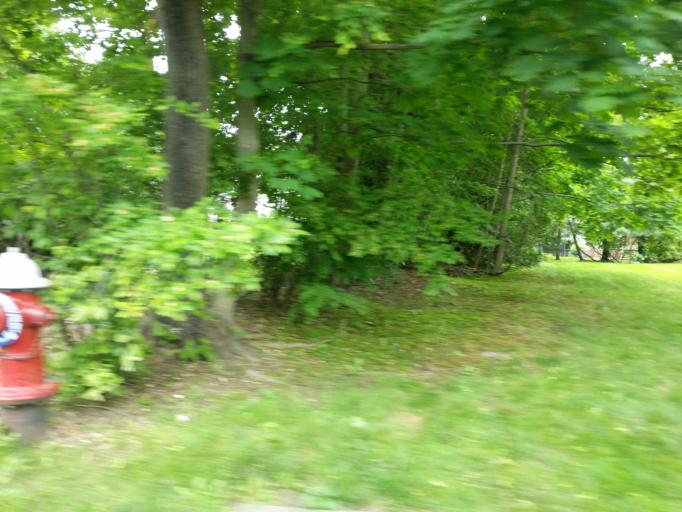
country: US
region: New York
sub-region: Nassau County
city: Hewlett
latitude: 40.6345
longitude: -73.6950
